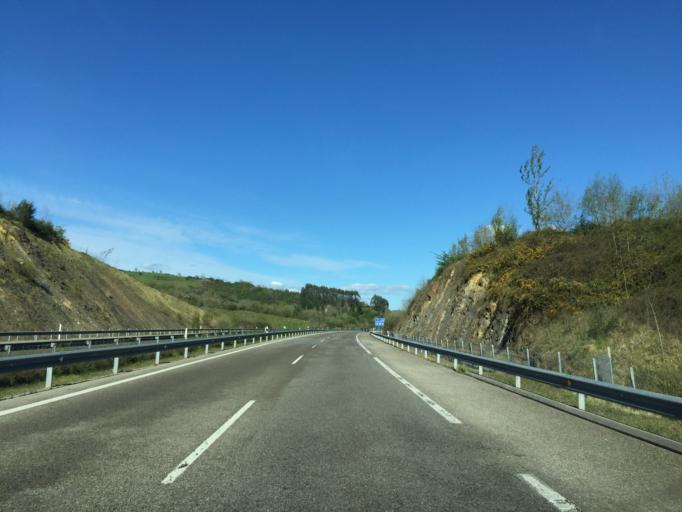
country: ES
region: Asturias
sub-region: Province of Asturias
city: Castandiello
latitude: 43.3543
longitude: -5.9354
